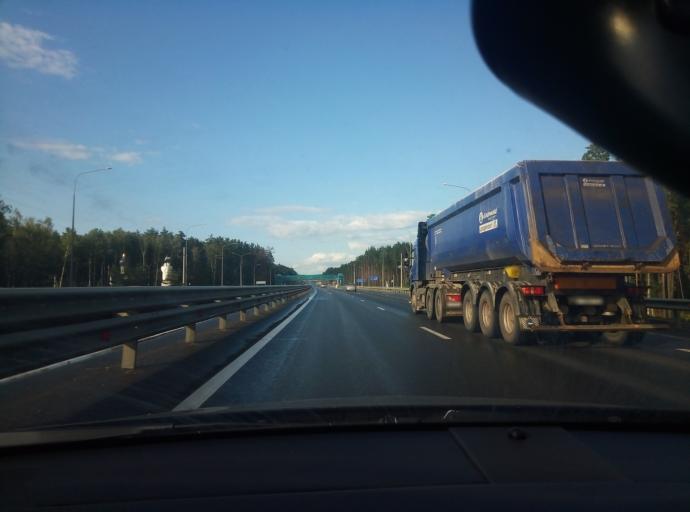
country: RU
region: Kaluga
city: Kurovskoye
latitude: 54.5650
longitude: 36.0481
